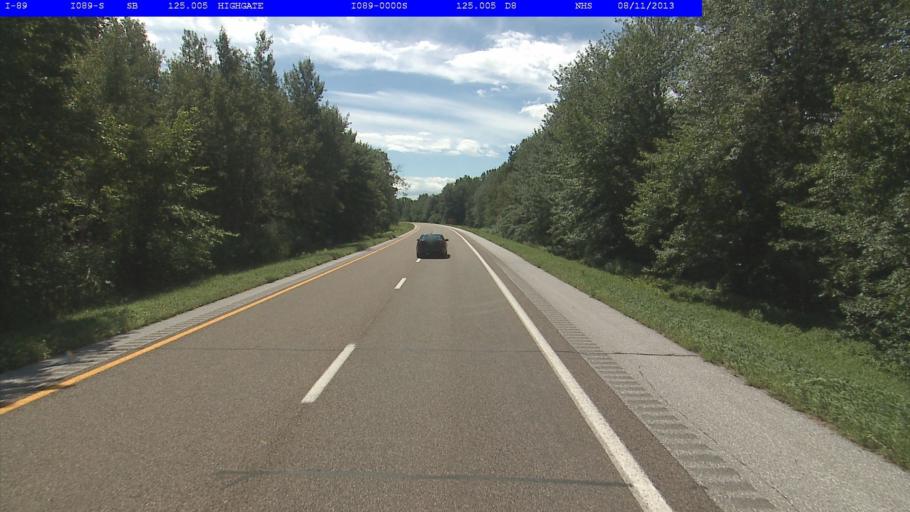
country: US
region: Vermont
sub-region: Franklin County
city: Swanton
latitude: 44.9451
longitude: -73.1145
